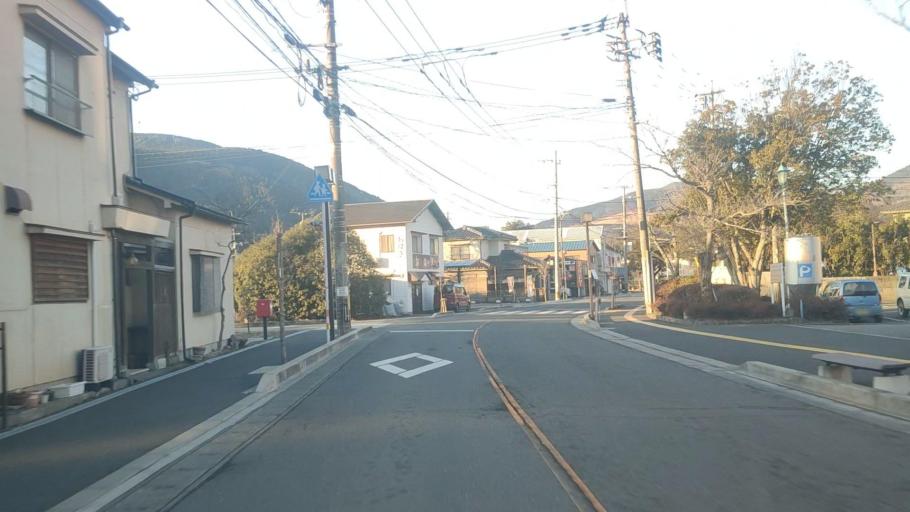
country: JP
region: Oita
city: Beppu
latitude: 33.2597
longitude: 131.3563
